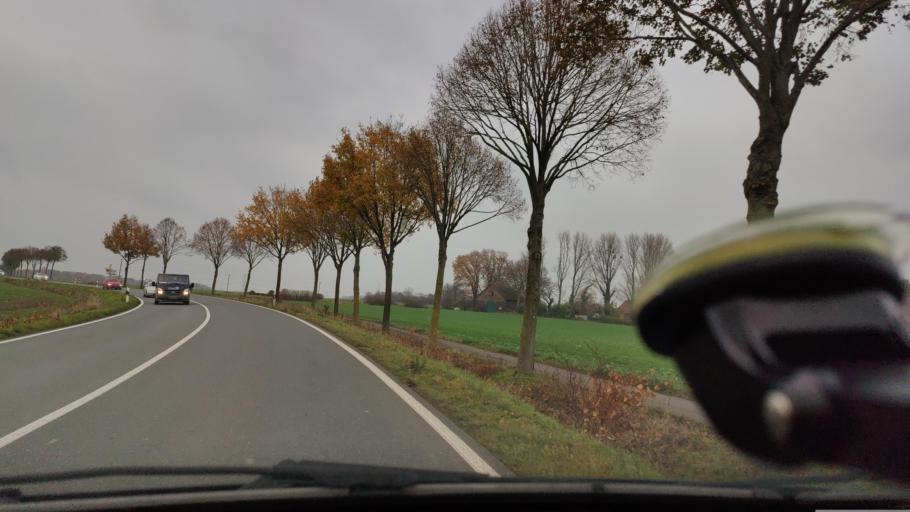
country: DE
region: North Rhine-Westphalia
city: Lunen
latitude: 51.6484
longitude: 7.5066
